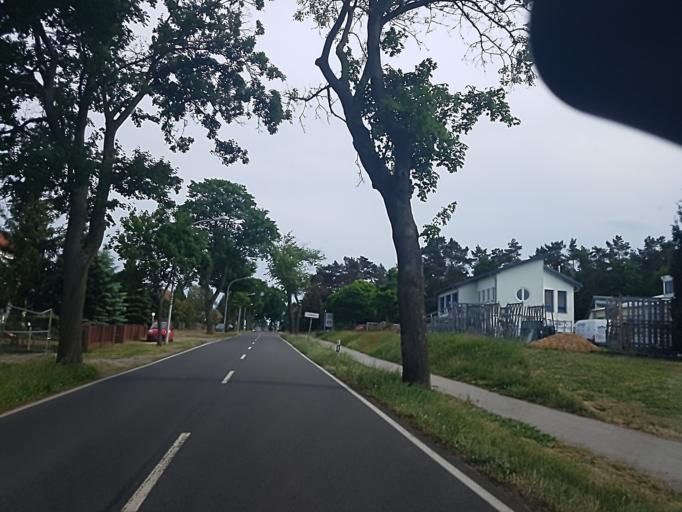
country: DE
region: Saxony-Anhalt
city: Nudersdorf
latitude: 51.9107
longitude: 12.6070
